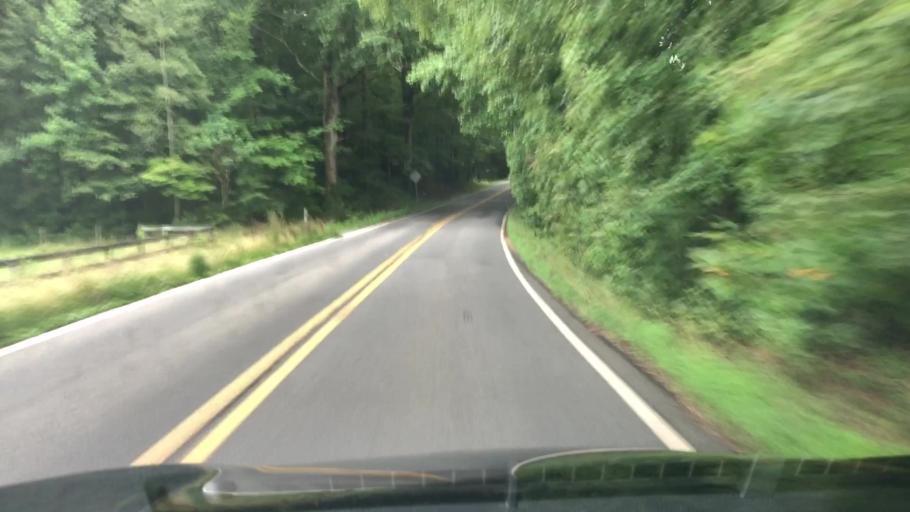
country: US
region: Virginia
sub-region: Fauquier County
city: Bealeton
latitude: 38.5401
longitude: -77.6122
